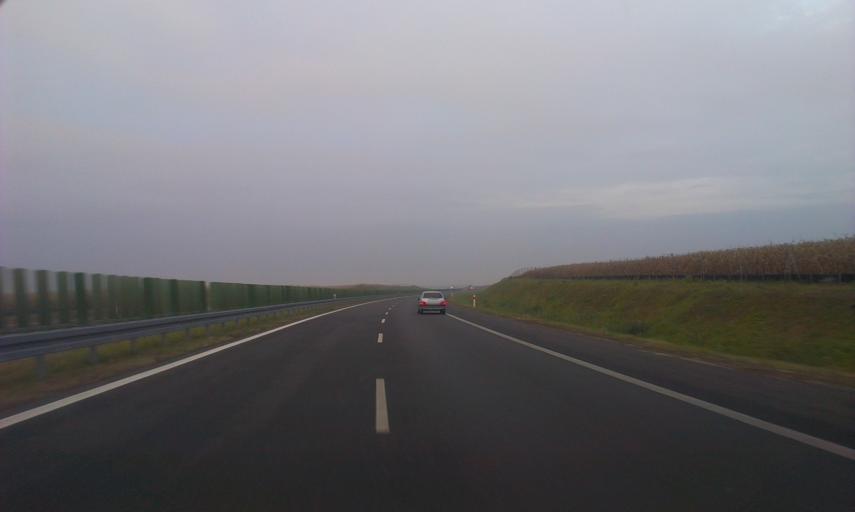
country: PL
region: Greater Poland Voivodeship
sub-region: Powiat poznanski
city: Zlotniki
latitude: 52.5135
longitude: 16.8120
